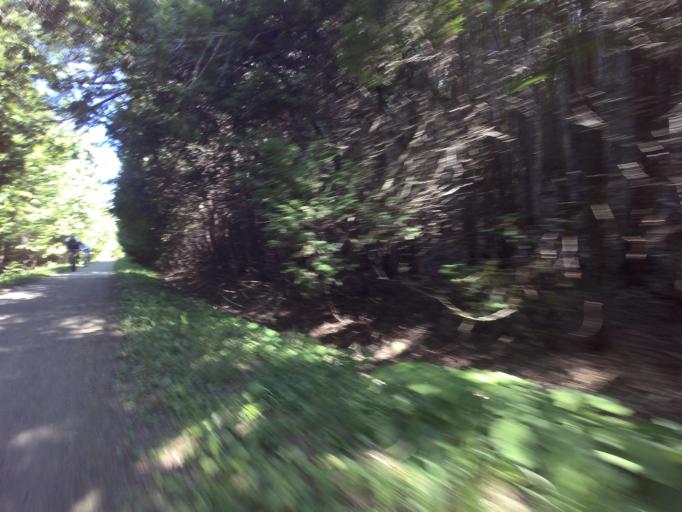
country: CA
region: Ontario
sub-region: Wellington County
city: Guelph
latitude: 43.7807
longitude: -80.3247
